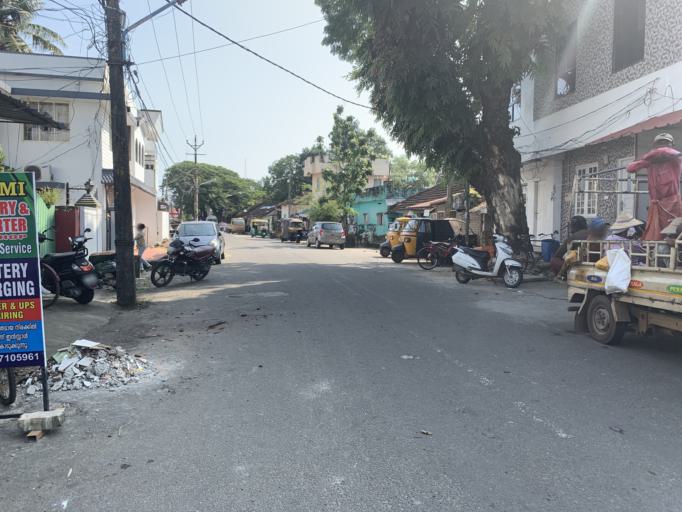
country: IN
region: Kerala
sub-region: Ernakulam
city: Cochin
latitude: 9.9629
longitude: 76.2563
